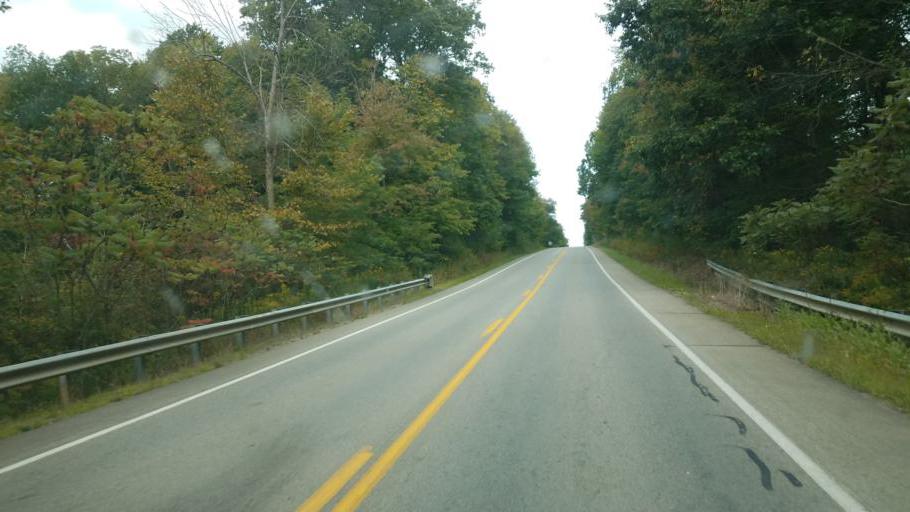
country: US
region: Pennsylvania
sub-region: Crawford County
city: Pymatuning Central
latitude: 41.4962
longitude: -80.4659
